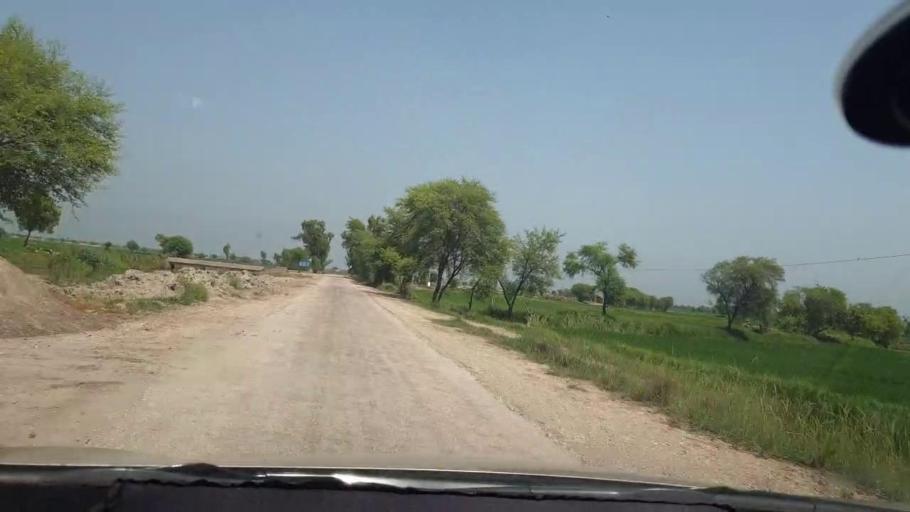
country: PK
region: Sindh
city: Kambar
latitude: 27.6858
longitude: 67.9331
